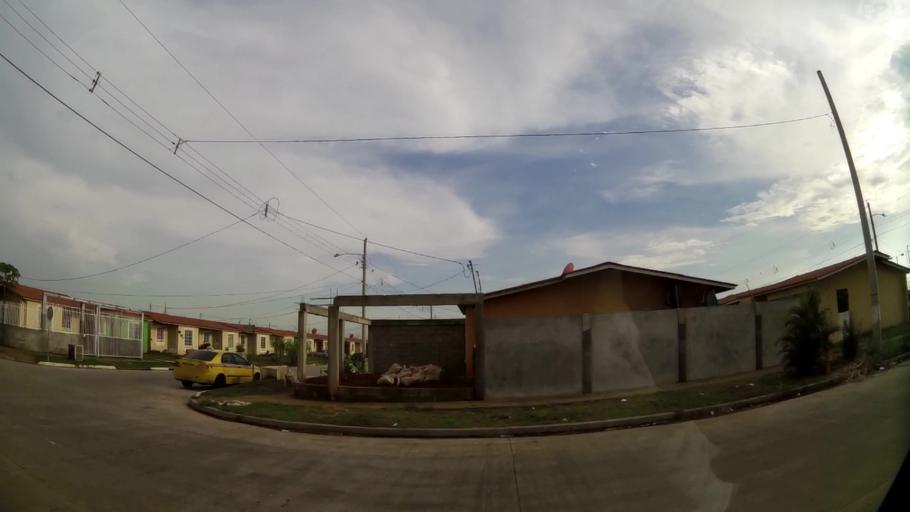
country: PA
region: Panama
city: Tocumen
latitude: 9.0761
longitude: -79.3572
